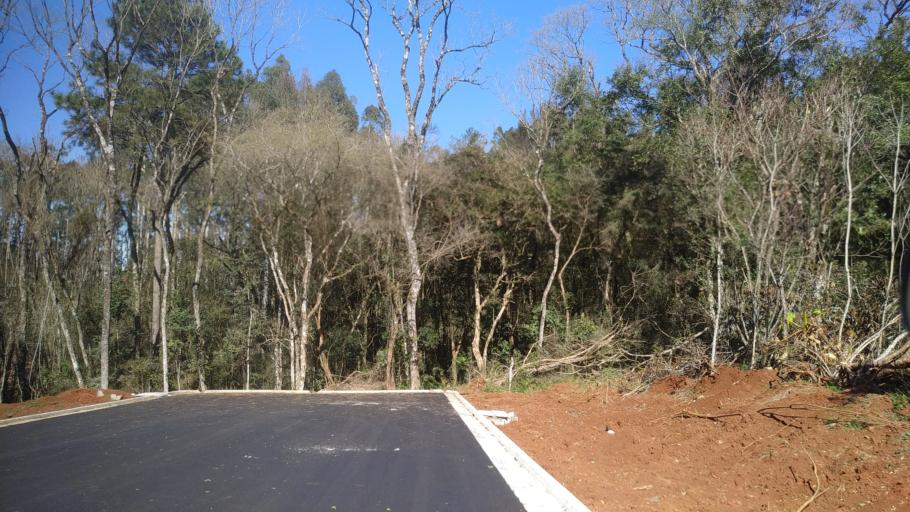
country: BR
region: Santa Catarina
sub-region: Chapeco
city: Chapeco
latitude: -27.0931
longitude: -52.7089
